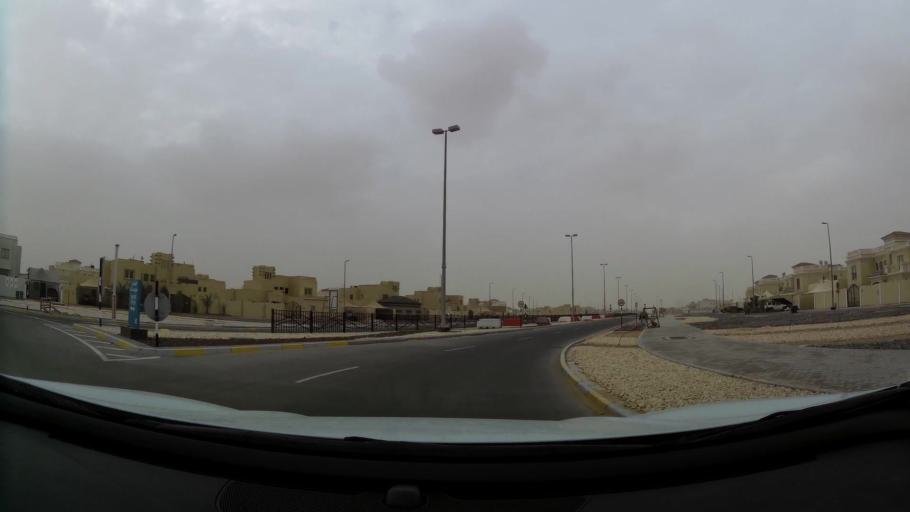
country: AE
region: Abu Dhabi
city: Abu Dhabi
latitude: 24.4495
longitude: 54.7401
